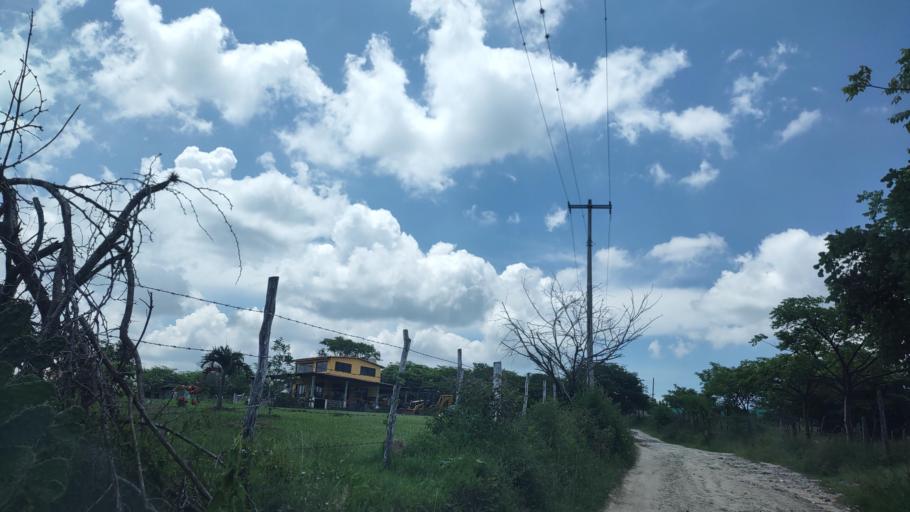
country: MX
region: Veracruz
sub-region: Emiliano Zapata
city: Dos Rios
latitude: 19.5001
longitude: -96.8125
